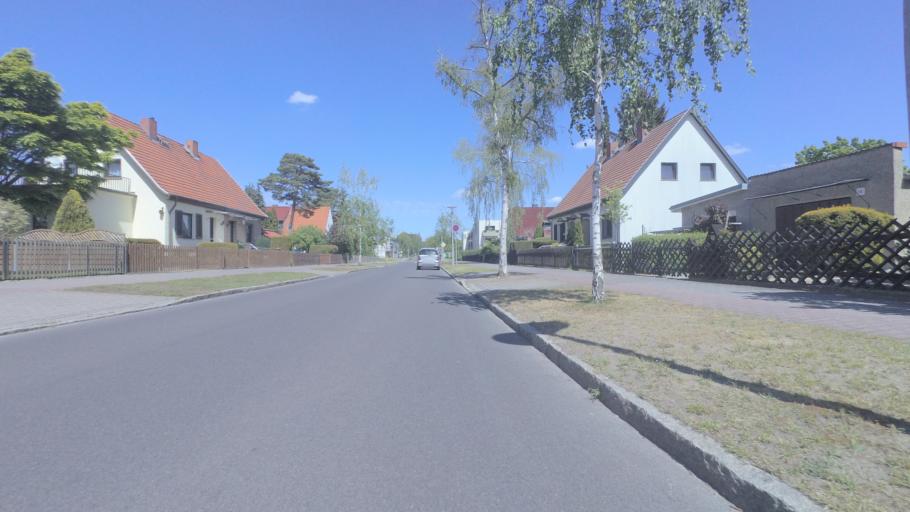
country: DE
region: Brandenburg
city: Rangsdorf
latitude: 52.3326
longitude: 13.4048
